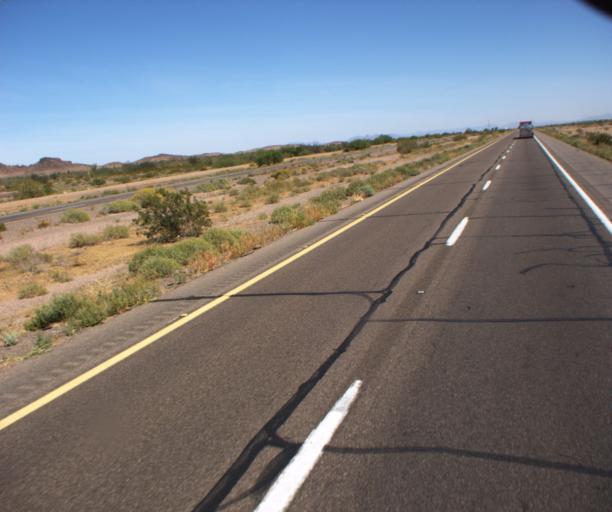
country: US
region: Arizona
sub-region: Maricopa County
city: Gila Bend
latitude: 32.8949
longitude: -113.0325
